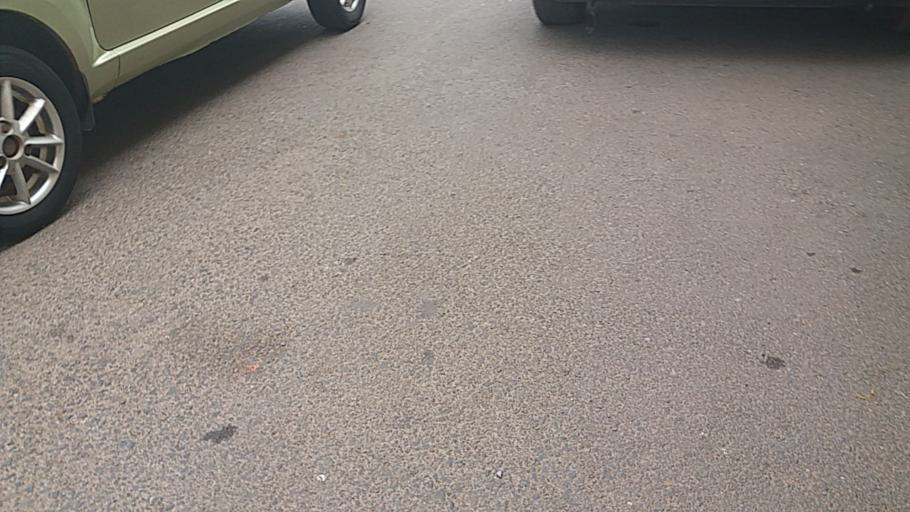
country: IN
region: Goa
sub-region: North Goa
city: Mapuca
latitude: 15.5880
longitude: 73.8137
